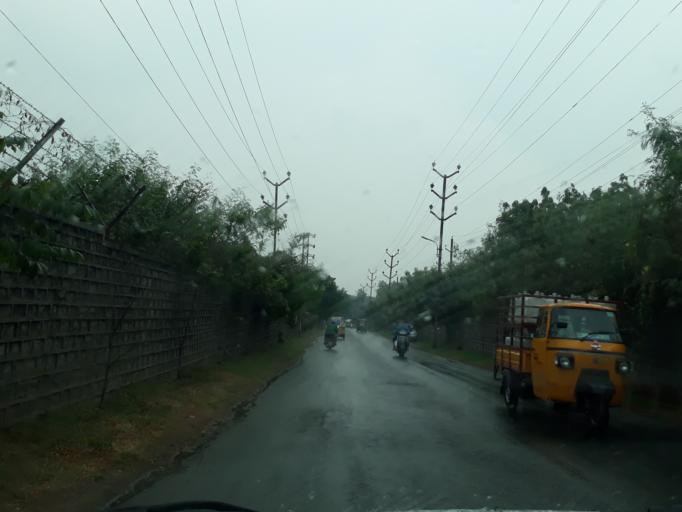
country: IN
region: Telangana
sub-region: Hyderabad
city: Malkajgiri
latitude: 17.4682
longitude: 78.5038
